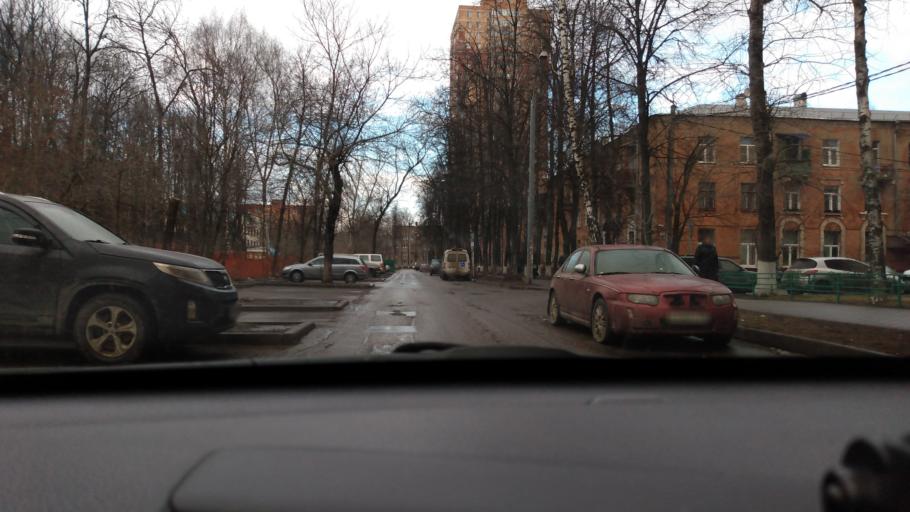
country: RU
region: Moskovskaya
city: Yubileyny
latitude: 55.9165
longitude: 37.8605
